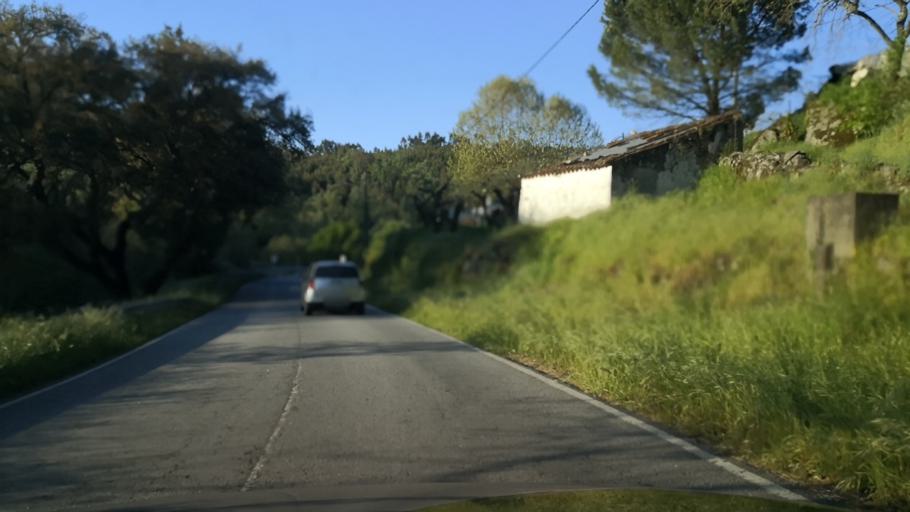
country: PT
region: Portalegre
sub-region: Marvao
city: Marvao
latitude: 39.3670
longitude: -7.4027
